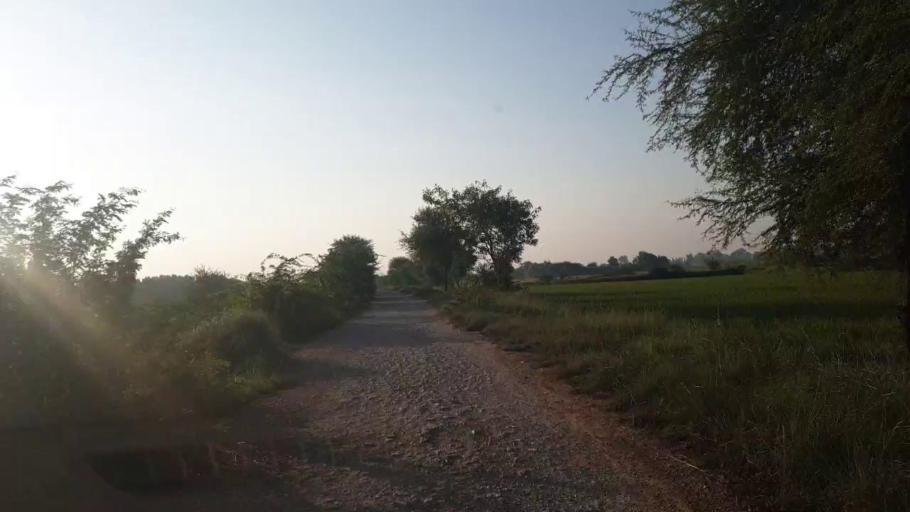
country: PK
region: Sindh
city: Badin
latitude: 24.6591
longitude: 68.7869
